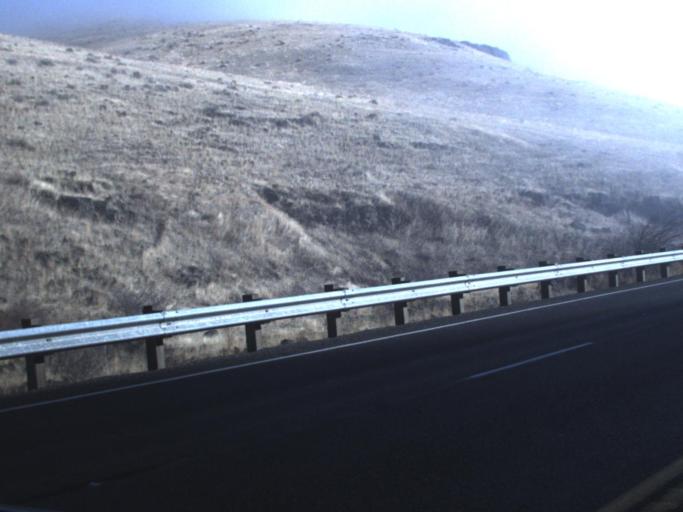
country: US
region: Washington
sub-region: Garfield County
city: Pomeroy
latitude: 46.4363
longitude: -117.3504
